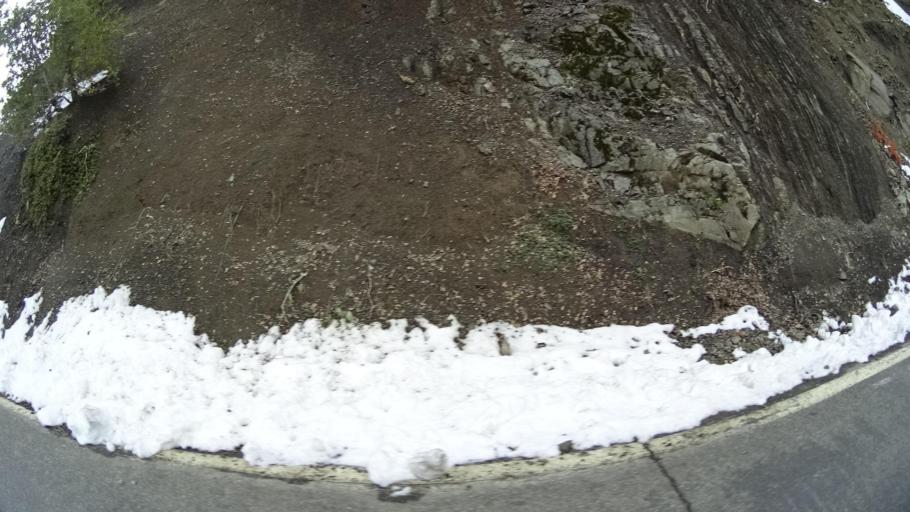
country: US
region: California
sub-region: Humboldt County
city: Willow Creek
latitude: 40.8790
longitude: -123.7584
